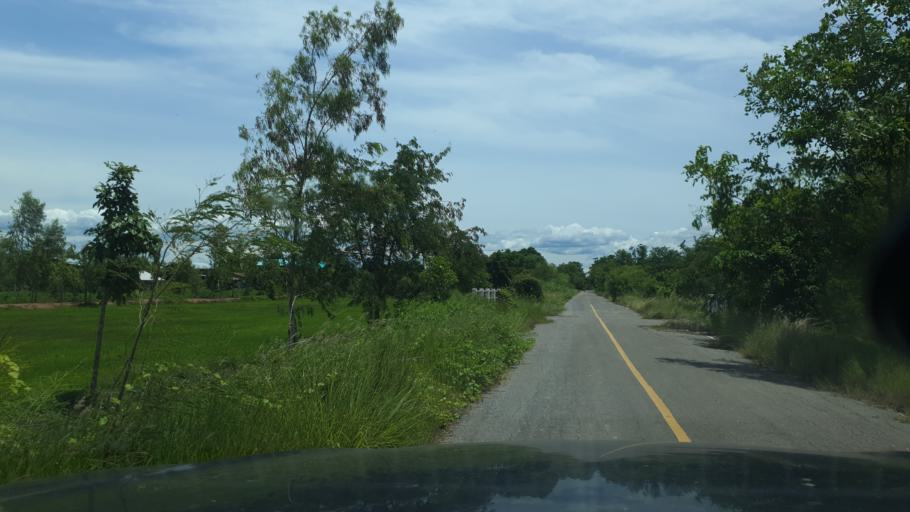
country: TH
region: Sukhothai
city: Ban Na
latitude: 17.1043
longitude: 99.6787
